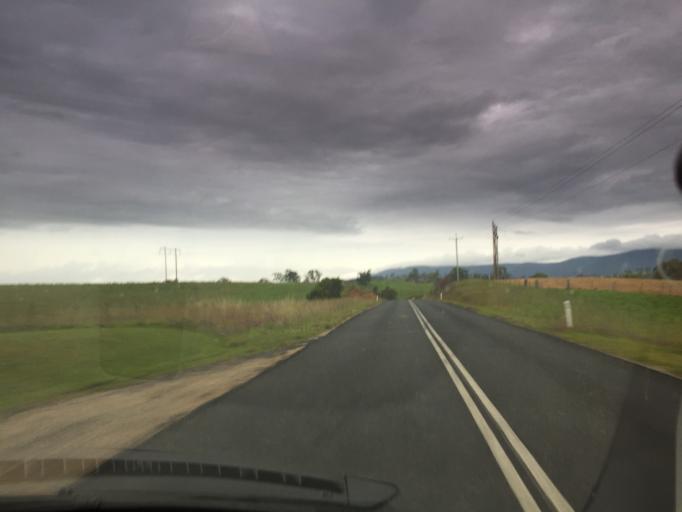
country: AU
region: New South Wales
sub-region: Bega Valley
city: Bega
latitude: -36.6514
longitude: 149.5833
